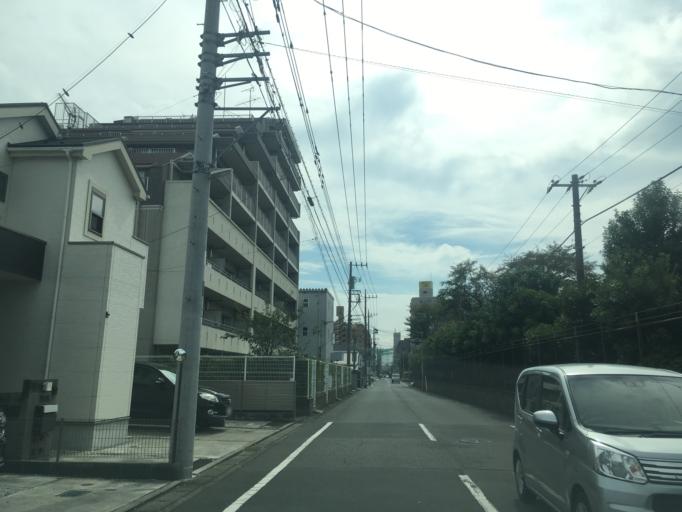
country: JP
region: Tokyo
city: Hachioji
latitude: 35.5828
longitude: 139.3491
